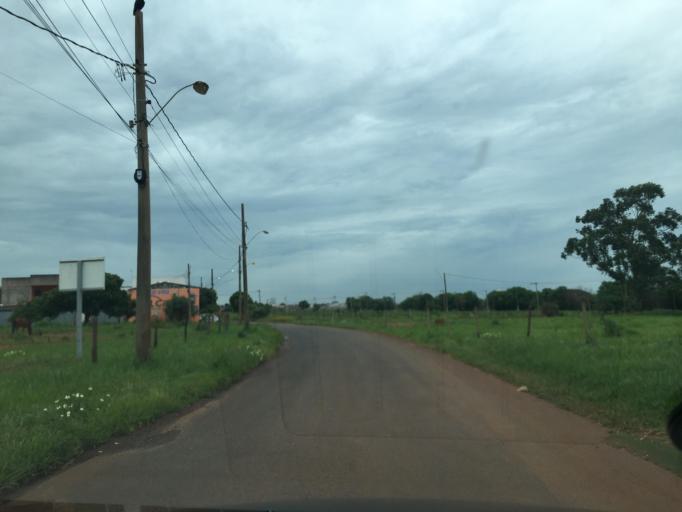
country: BR
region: Minas Gerais
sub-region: Uberlandia
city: Uberlandia
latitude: -18.8642
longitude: -48.2223
